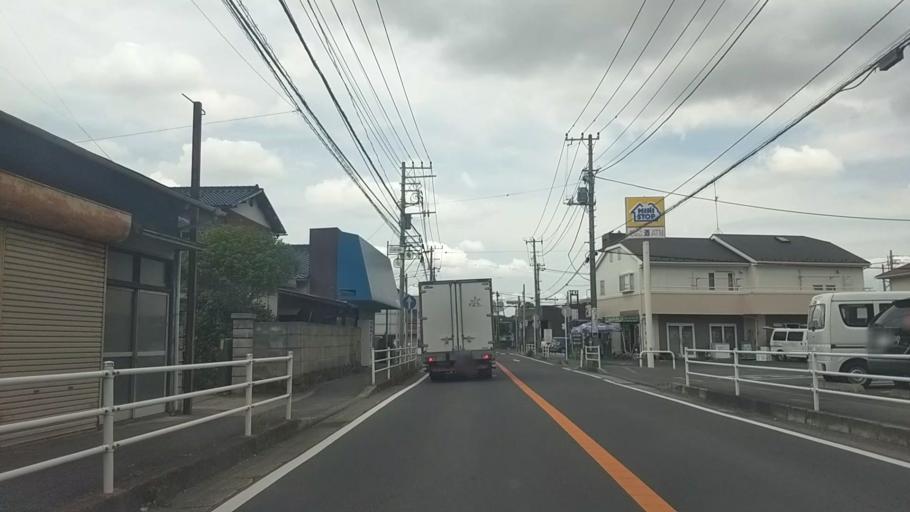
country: JP
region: Kanagawa
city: Fujisawa
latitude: 35.3268
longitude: 139.5088
